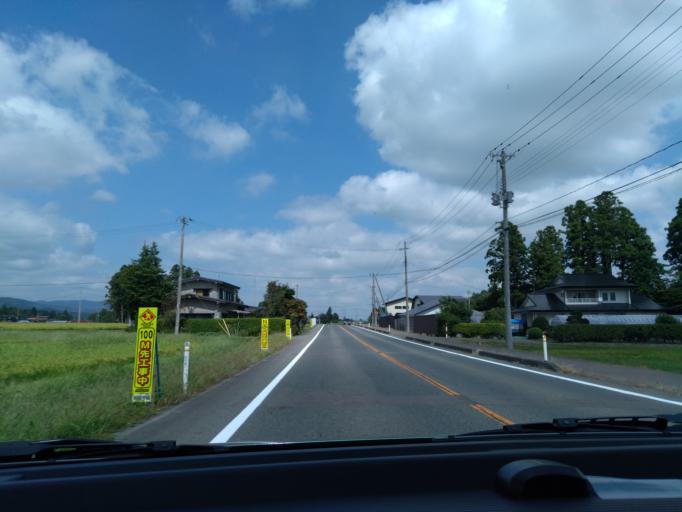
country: JP
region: Iwate
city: Hanamaki
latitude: 39.4319
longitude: 141.0929
